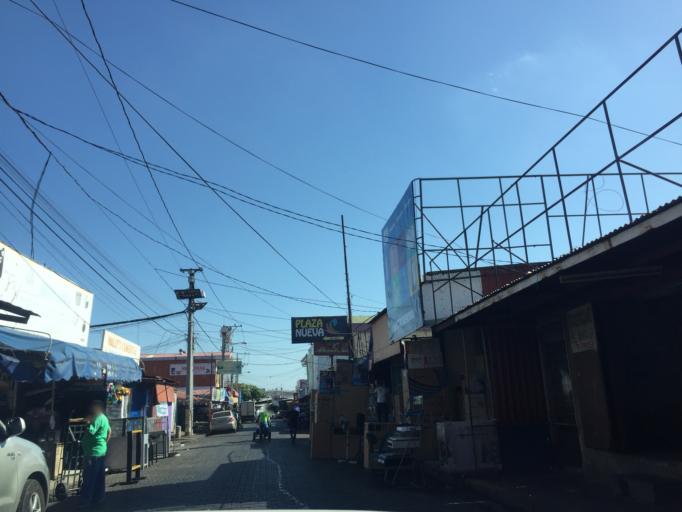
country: NI
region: Managua
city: Managua
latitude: 12.1457
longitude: -86.2590
